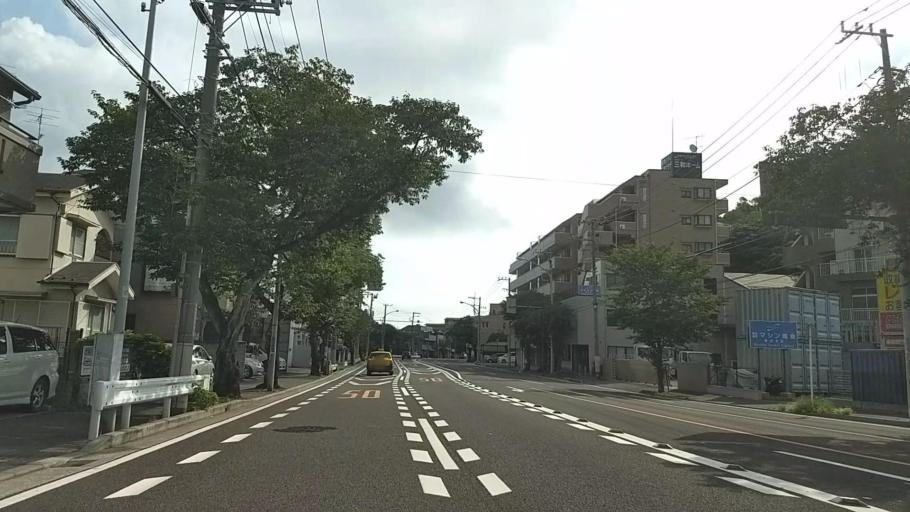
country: JP
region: Kanagawa
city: Yokohama
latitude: 35.4195
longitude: 139.6517
